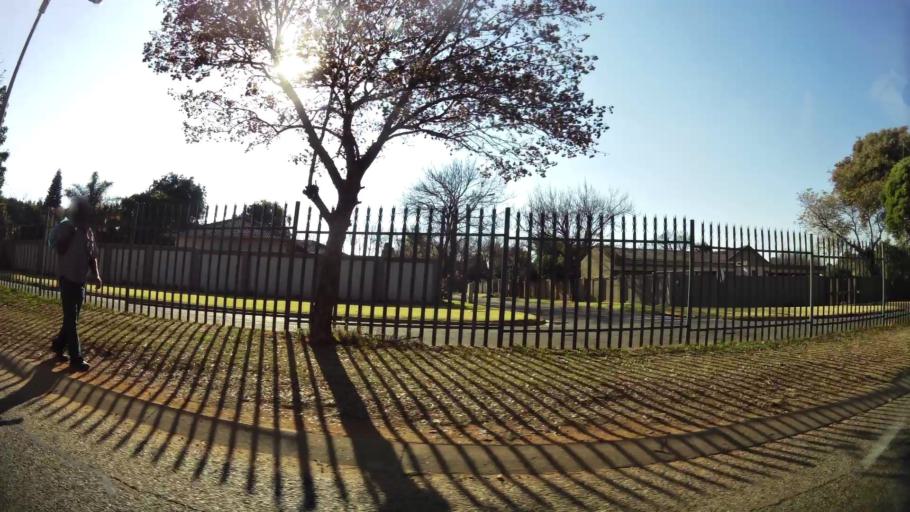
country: ZA
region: Gauteng
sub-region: City of Johannesburg Metropolitan Municipality
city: Modderfontein
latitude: -26.1559
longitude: 28.1539
